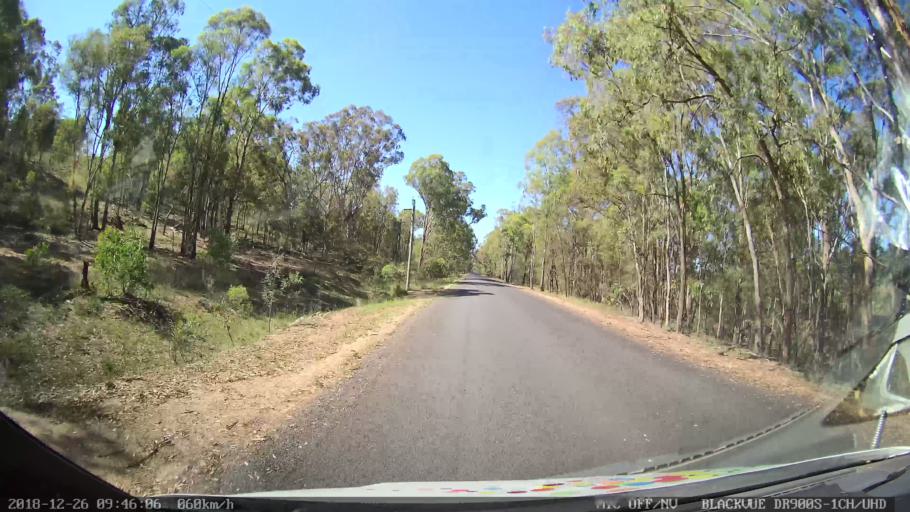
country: AU
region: New South Wales
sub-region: Mid-Western Regional
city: Kandos
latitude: -32.9666
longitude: 150.1058
